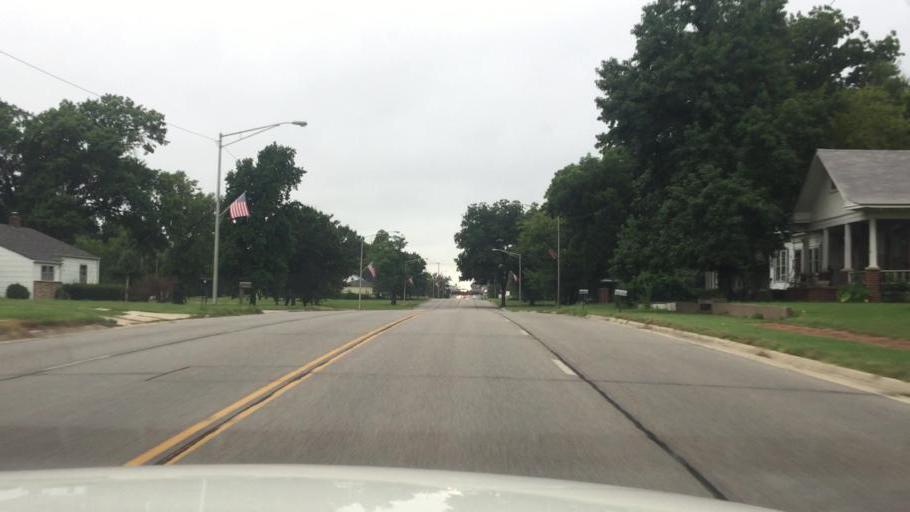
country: US
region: Kansas
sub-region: Montgomery County
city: Coffeyville
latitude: 37.0329
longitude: -95.6078
